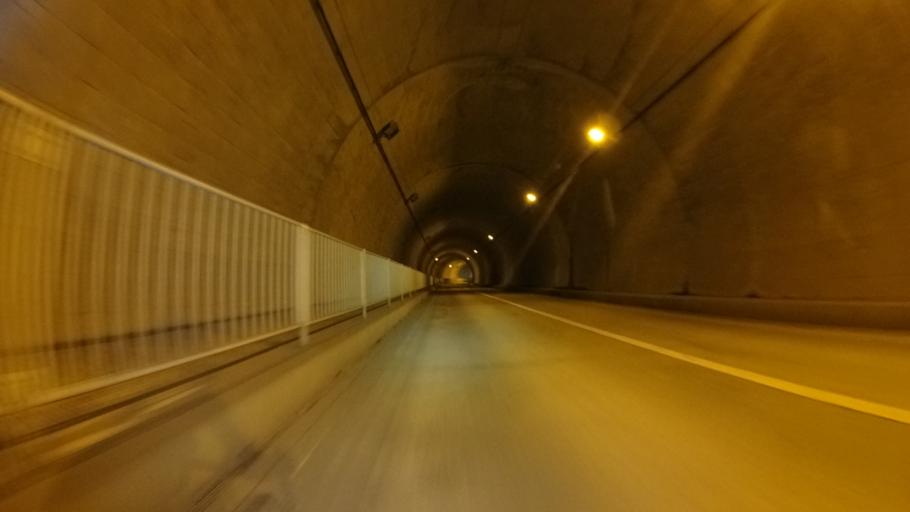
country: JP
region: Yamanashi
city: Uenohara
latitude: 35.6703
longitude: 139.0985
